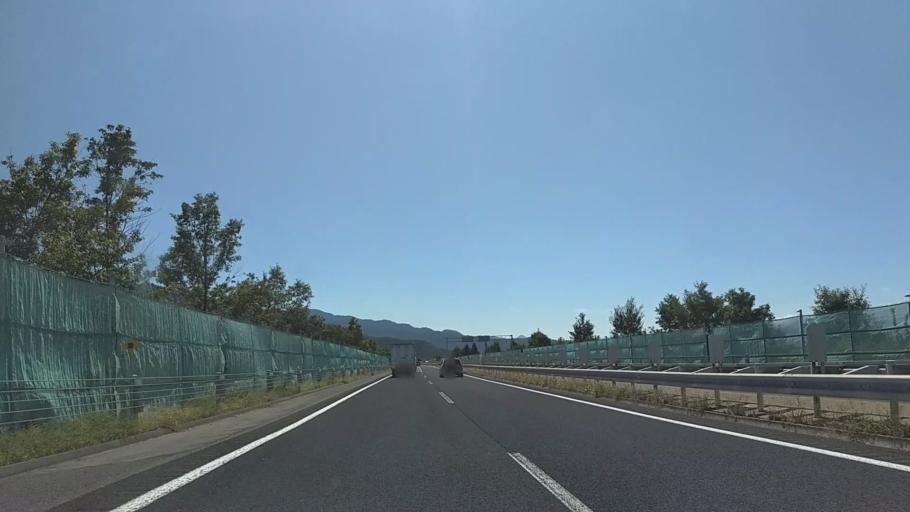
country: JP
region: Nagano
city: Suzaka
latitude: 36.6426
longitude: 138.2778
